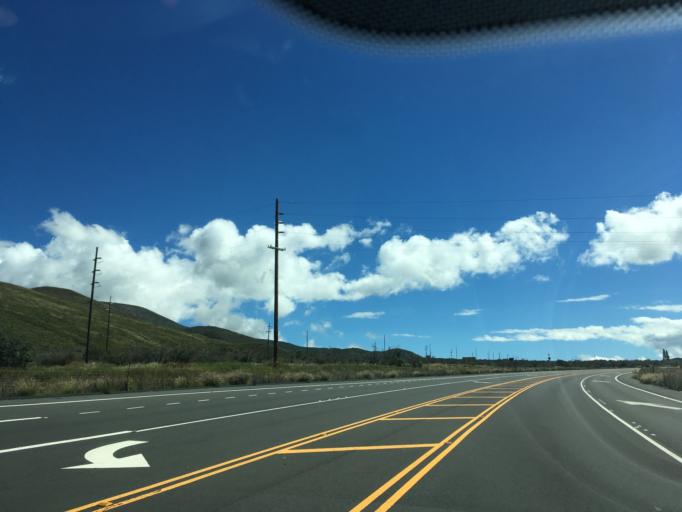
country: US
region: Hawaii
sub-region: Hawaii County
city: Waimea
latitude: 19.7587
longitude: -155.5324
